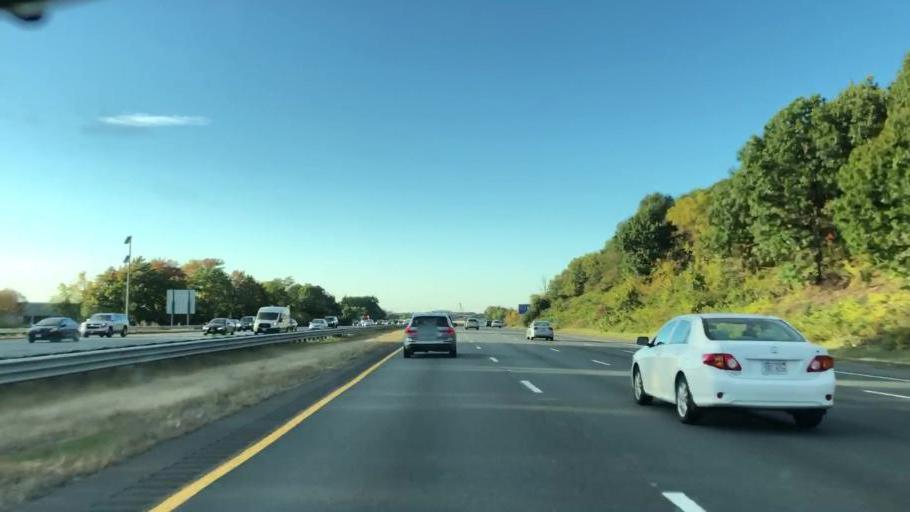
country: US
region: Massachusetts
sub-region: Middlesex County
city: Reading
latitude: 42.5125
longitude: -71.1265
